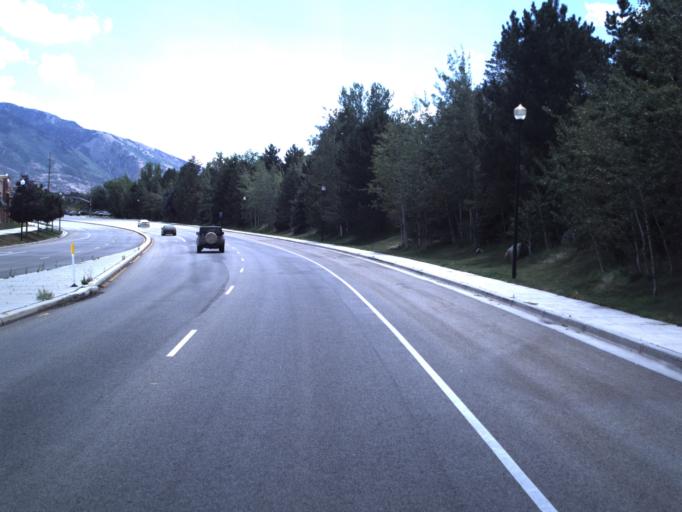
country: US
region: Utah
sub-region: Salt Lake County
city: Sandy Hills
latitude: 40.5836
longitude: -111.8637
